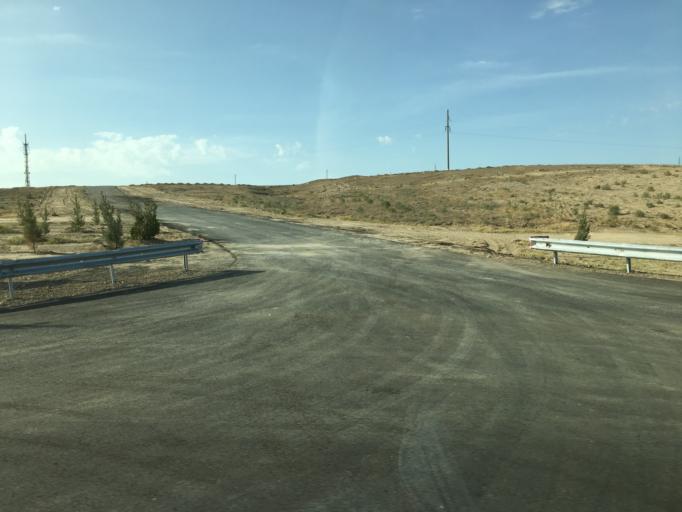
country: TM
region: Balkan
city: Turkmenbasy
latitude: 40.0467
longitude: 52.9464
